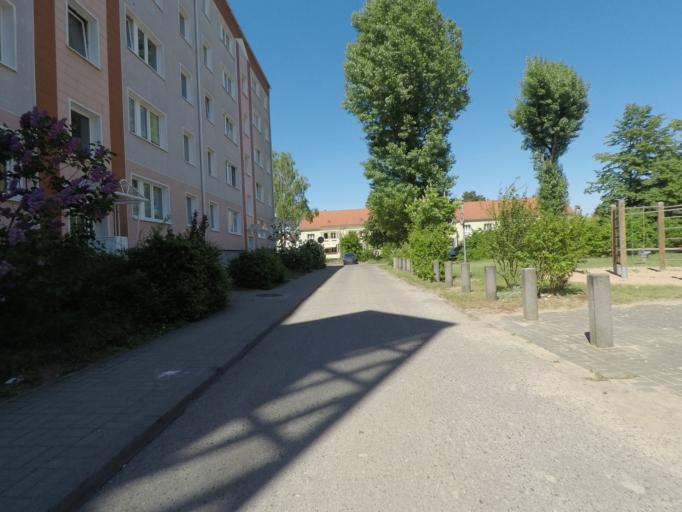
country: DE
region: Brandenburg
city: Melchow
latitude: 52.8359
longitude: 13.7447
